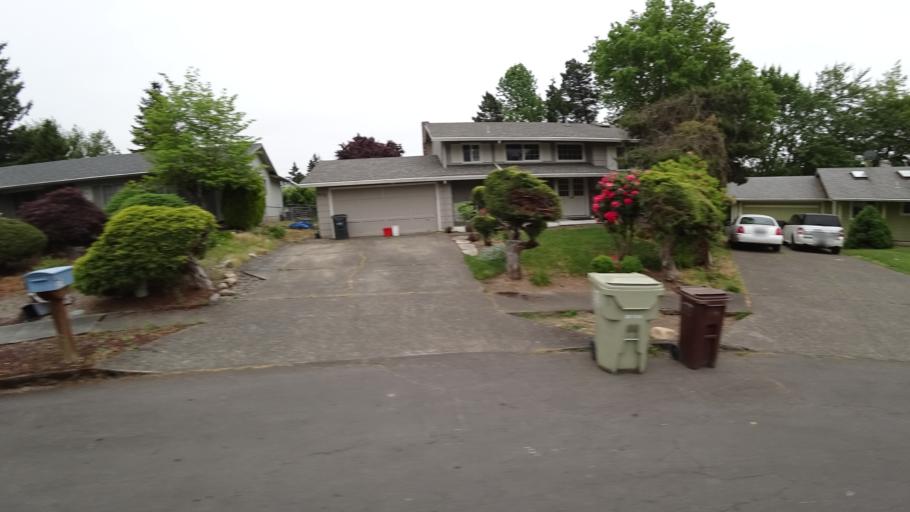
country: US
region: Oregon
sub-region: Washington County
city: Bethany
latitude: 45.5454
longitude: -122.8647
